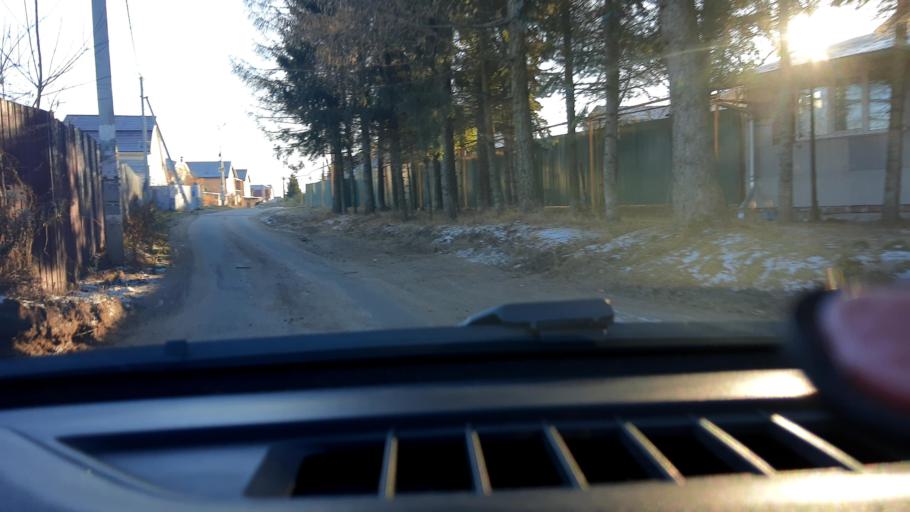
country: RU
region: Nizjnij Novgorod
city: Burevestnik
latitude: 56.2002
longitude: 43.8634
